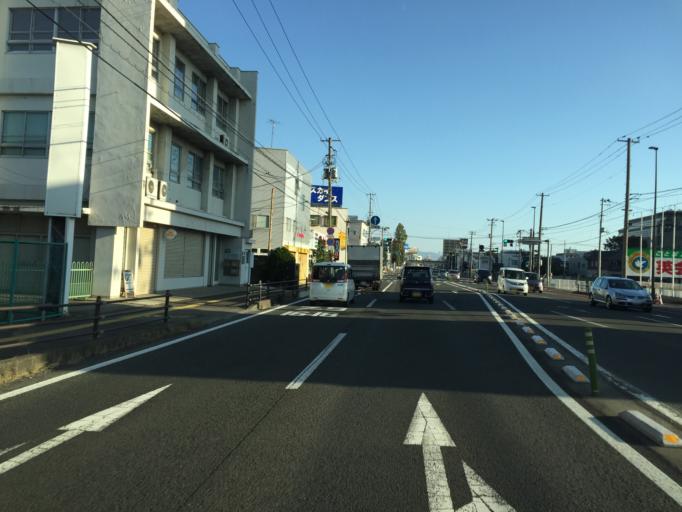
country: JP
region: Fukushima
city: Fukushima-shi
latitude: 37.7635
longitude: 140.4775
